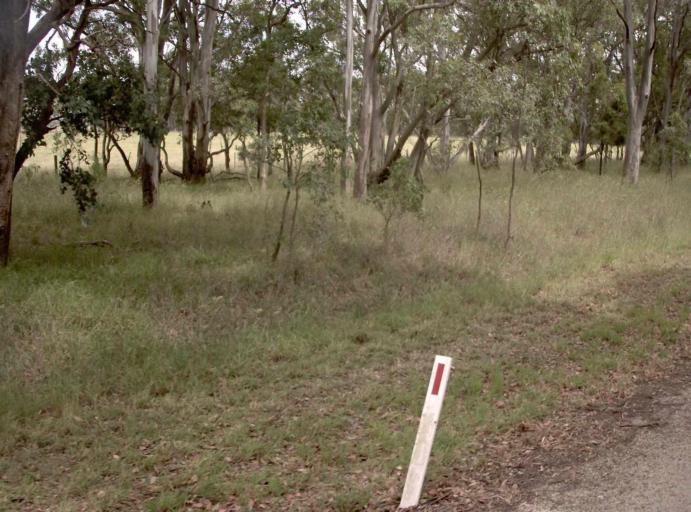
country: AU
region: Victoria
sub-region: Wellington
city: Sale
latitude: -37.8898
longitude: 147.0668
